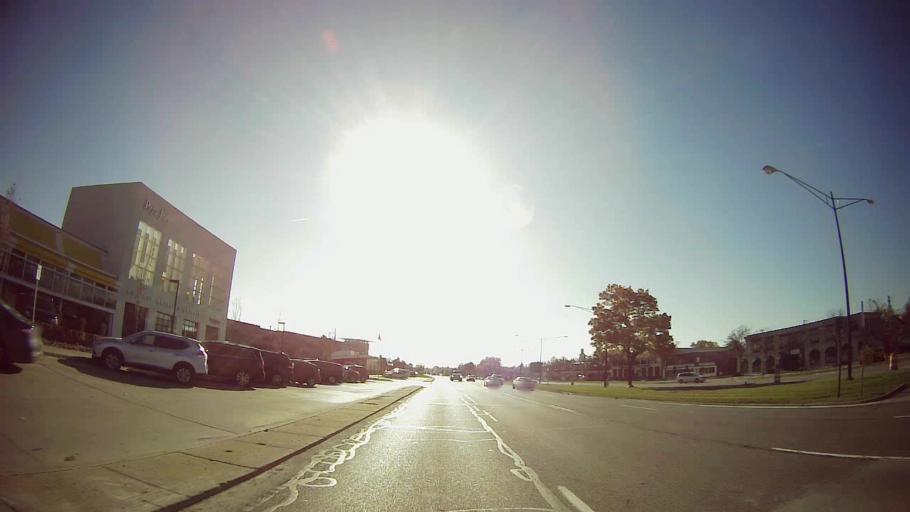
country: US
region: Michigan
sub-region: Oakland County
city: Birmingham
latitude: 42.5411
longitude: -83.2079
